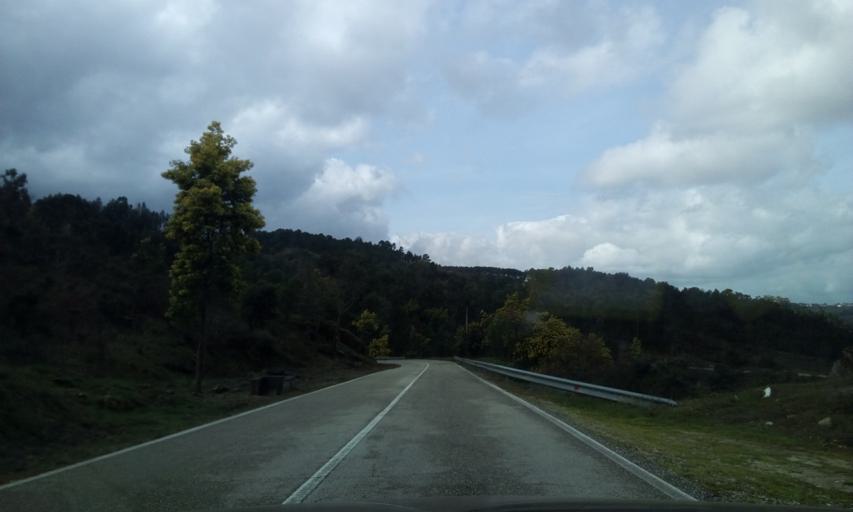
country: PT
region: Viseu
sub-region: Satao
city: Satao
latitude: 40.6640
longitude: -7.6715
